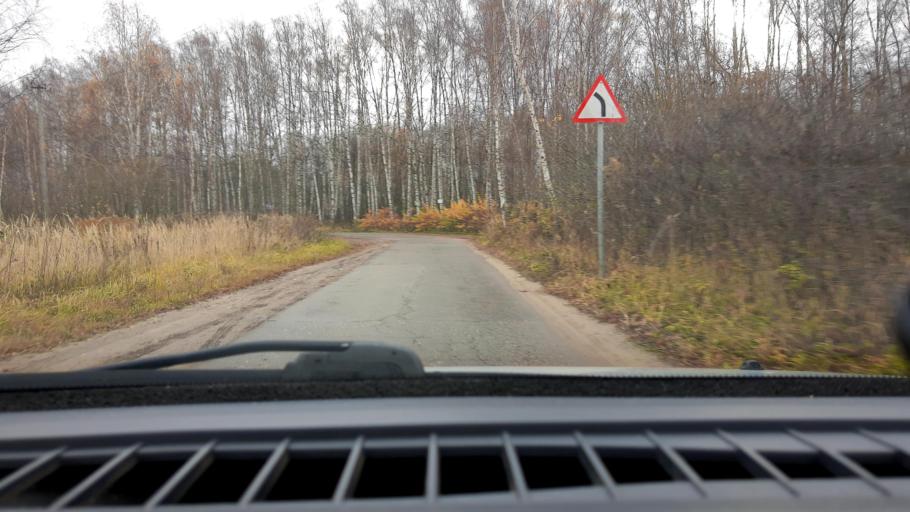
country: RU
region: Nizjnij Novgorod
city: Afonino
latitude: 56.1920
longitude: 44.0986
